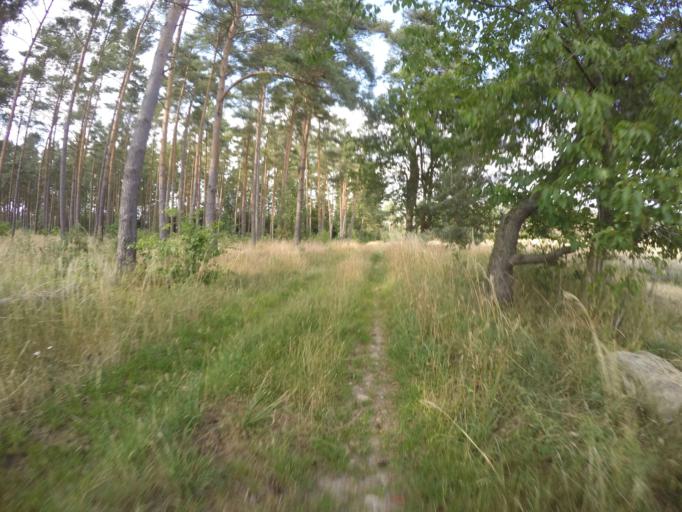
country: DE
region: Lower Saxony
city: Dahlem
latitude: 53.2350
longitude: 10.7326
